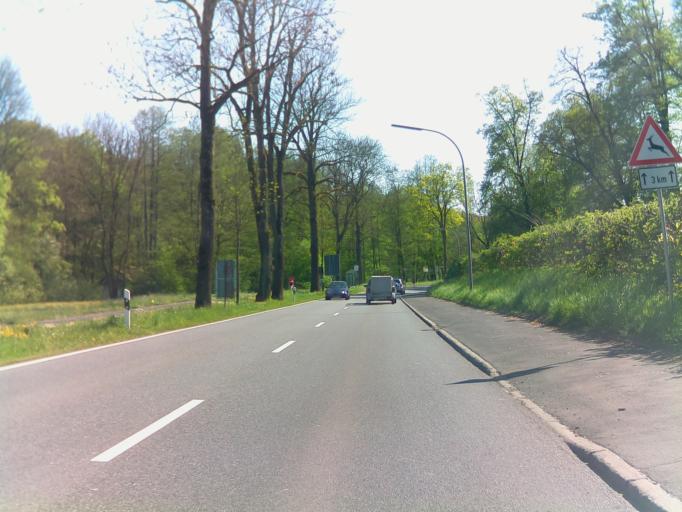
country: DE
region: Hesse
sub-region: Regierungsbezirk Darmstadt
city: Birstein
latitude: 50.3504
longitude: 9.3098
